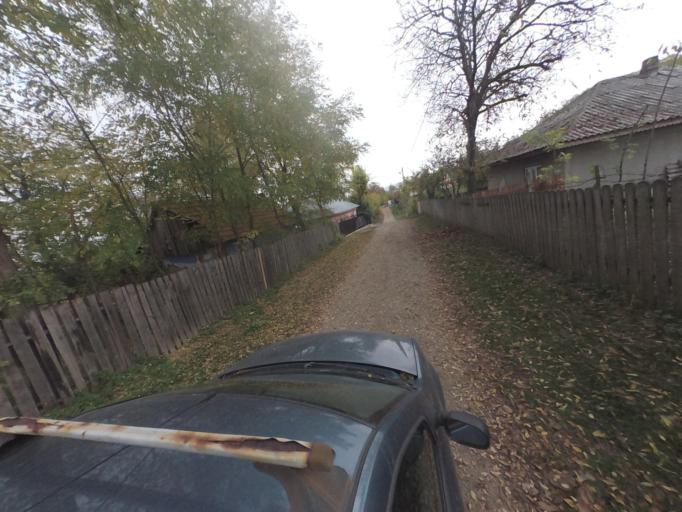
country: RO
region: Vaslui
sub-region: Comuna Bacesti
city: Bacesti
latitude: 46.8339
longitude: 27.2291
